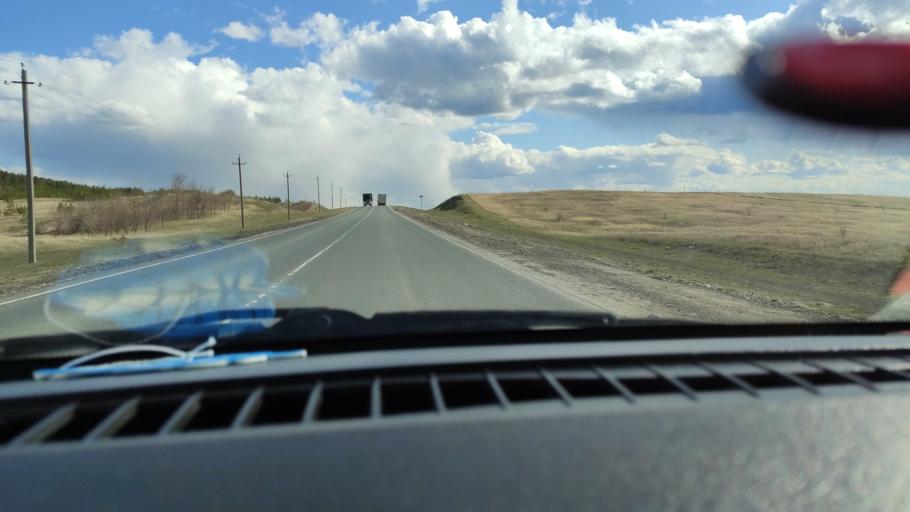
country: RU
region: Saratov
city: Alekseyevka
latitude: 52.3003
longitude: 47.9273
